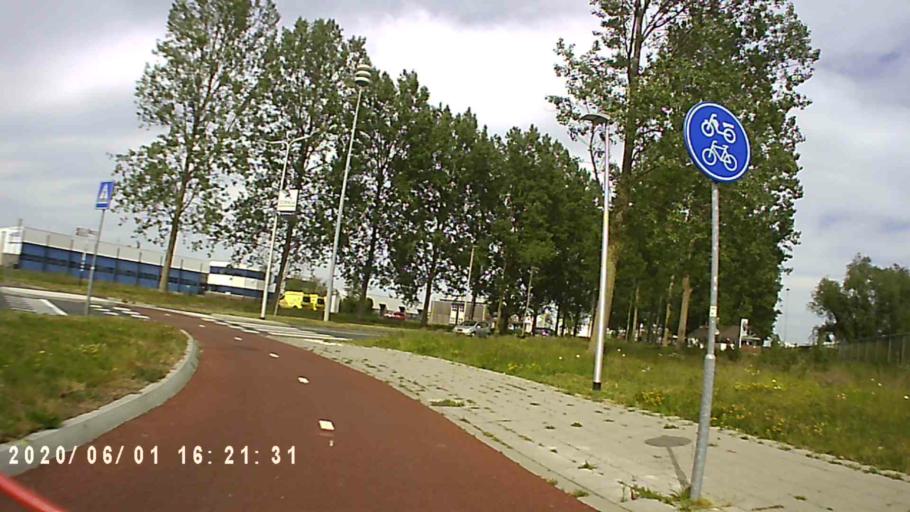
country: NL
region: Friesland
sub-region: Gemeente Leeuwarden
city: Camminghaburen
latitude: 53.1955
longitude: 5.8486
